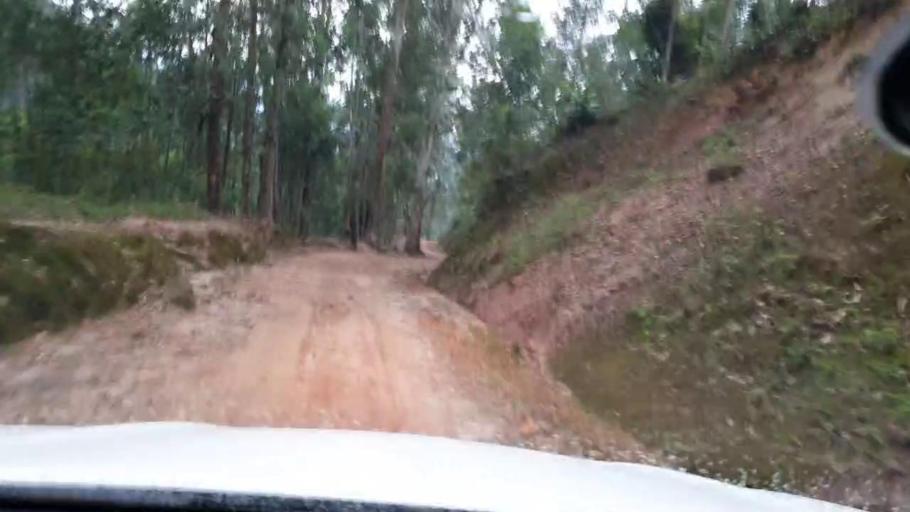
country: RW
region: Western Province
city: Cyangugu
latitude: -2.4111
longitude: 29.1984
